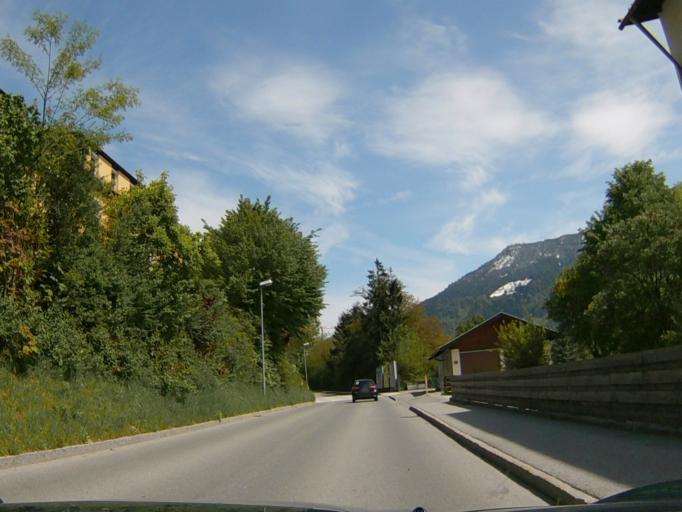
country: AT
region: Tyrol
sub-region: Politischer Bezirk Schwaz
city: Jenbach
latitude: 47.3914
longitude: 11.7613
